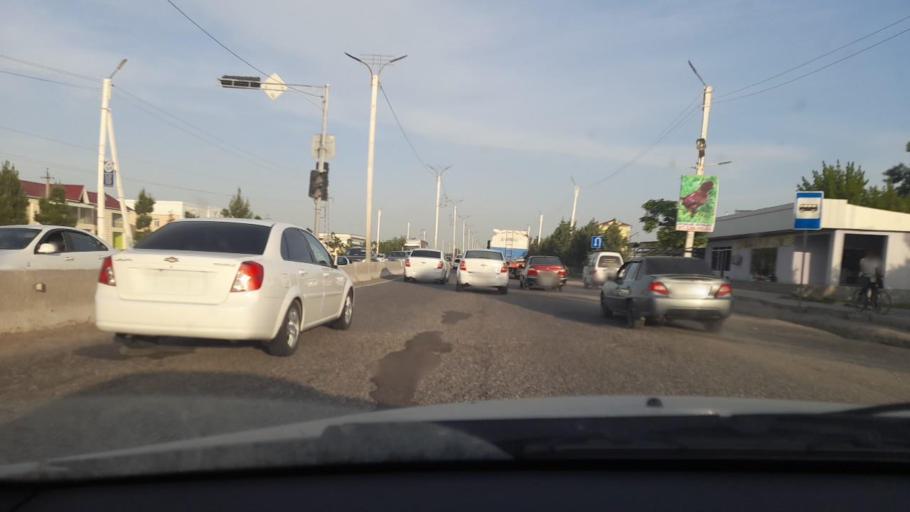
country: KZ
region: Ongtustik Qazaqstan
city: Myrzakent
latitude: 40.5477
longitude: 68.4071
